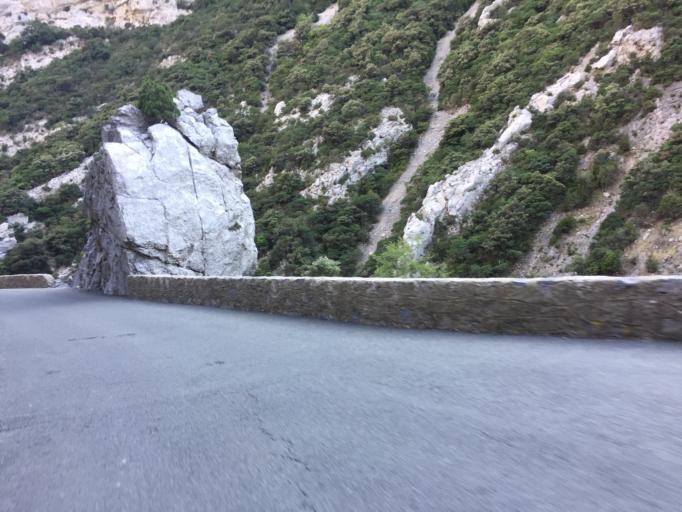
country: FR
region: Languedoc-Roussillon
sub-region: Departement des Pyrenees-Orientales
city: Saint-Paul-de-Fenouillet
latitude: 42.8446
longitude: 2.4785
